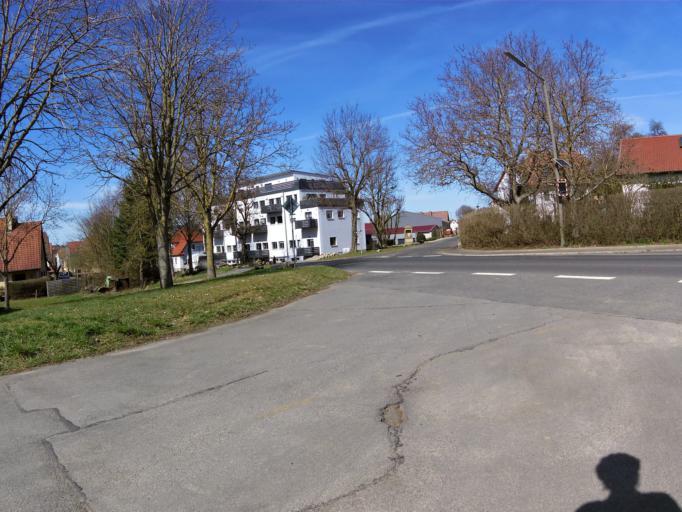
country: DE
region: Bavaria
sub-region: Regierungsbezirk Unterfranken
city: Biebelried
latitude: 49.7950
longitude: 10.1086
